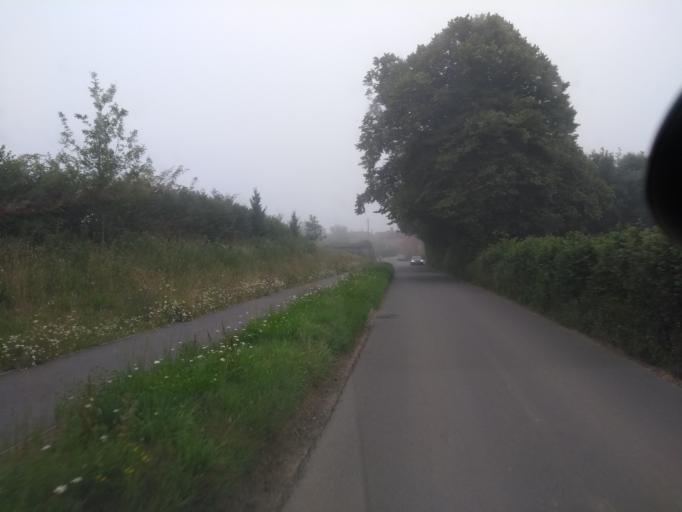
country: GB
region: England
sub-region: Dorset
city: Bridport
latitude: 50.7706
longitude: -2.7736
